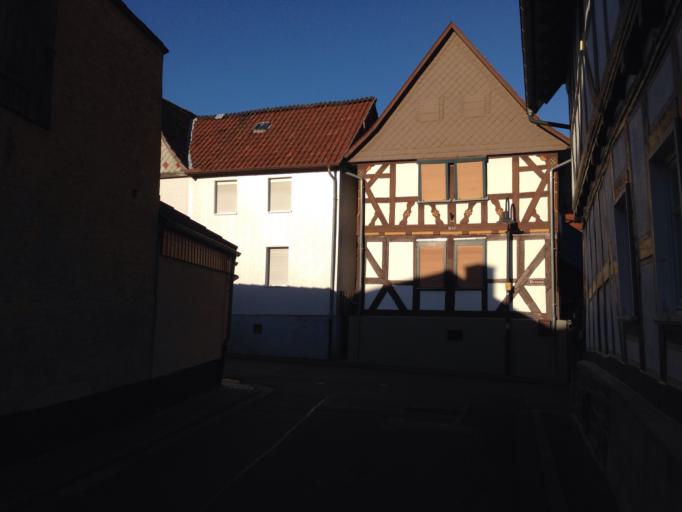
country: DE
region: Hesse
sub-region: Regierungsbezirk Giessen
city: Lich
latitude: 50.5544
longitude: 8.7960
